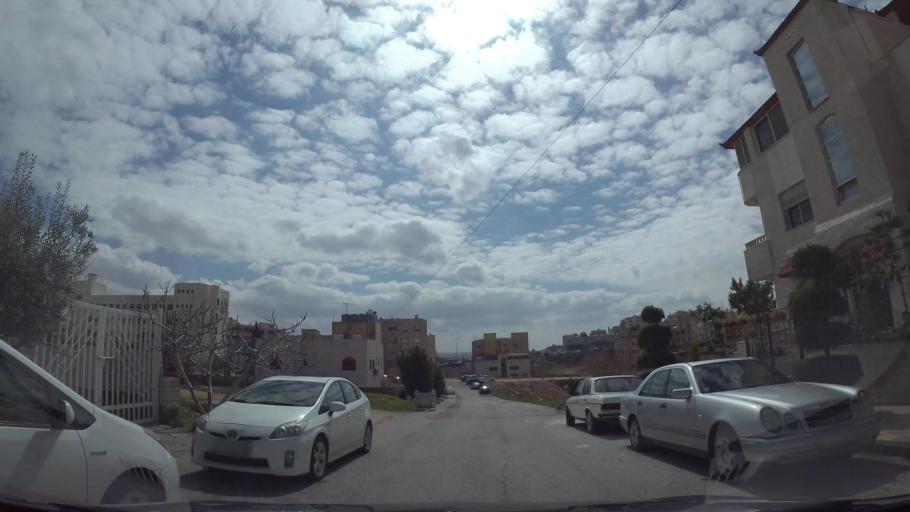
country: JO
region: Amman
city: Amman
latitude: 31.9940
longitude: 35.9139
